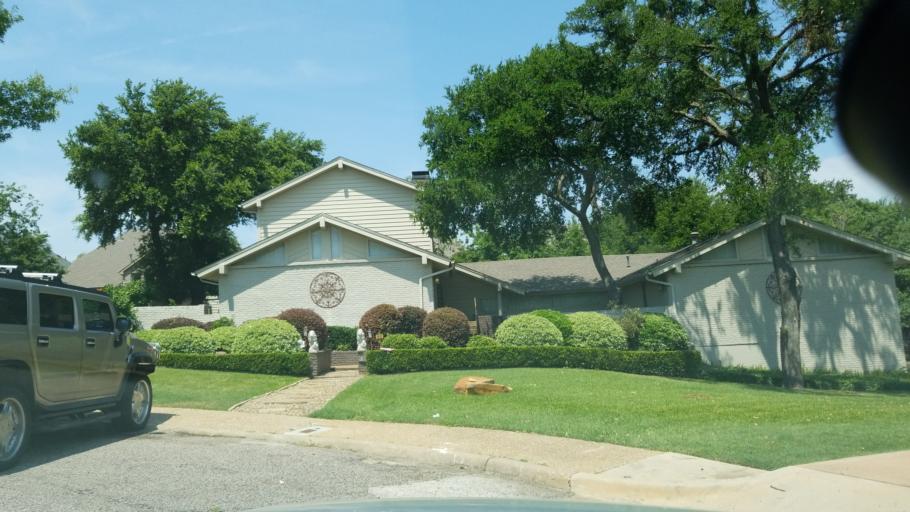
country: US
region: Texas
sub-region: Dallas County
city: Irving
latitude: 32.8491
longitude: -96.9412
